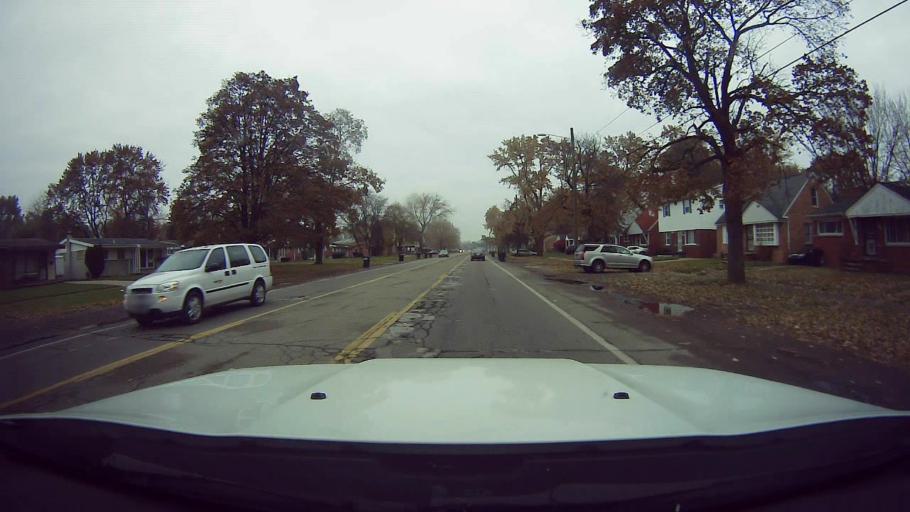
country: US
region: Michigan
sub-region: Oakland County
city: Southfield
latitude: 42.4387
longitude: -83.2586
